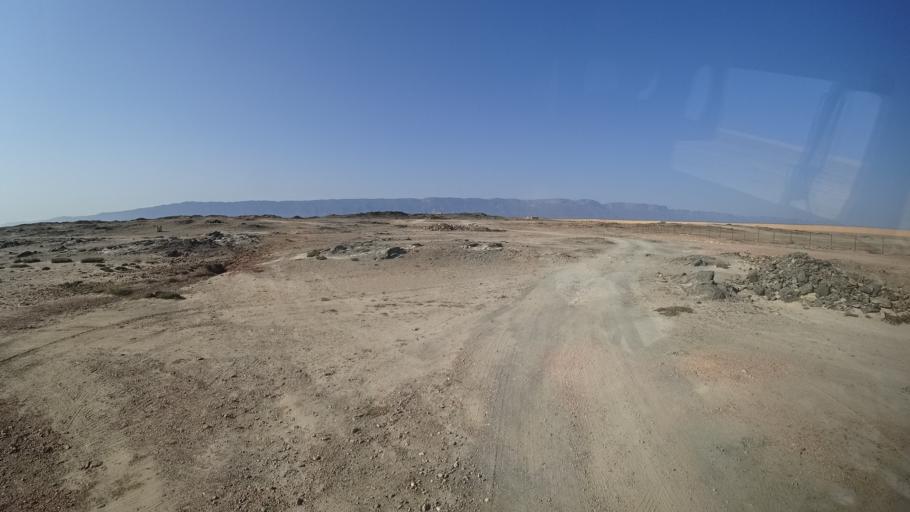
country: OM
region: Zufar
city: Salalah
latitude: 16.9454
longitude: 54.7996
